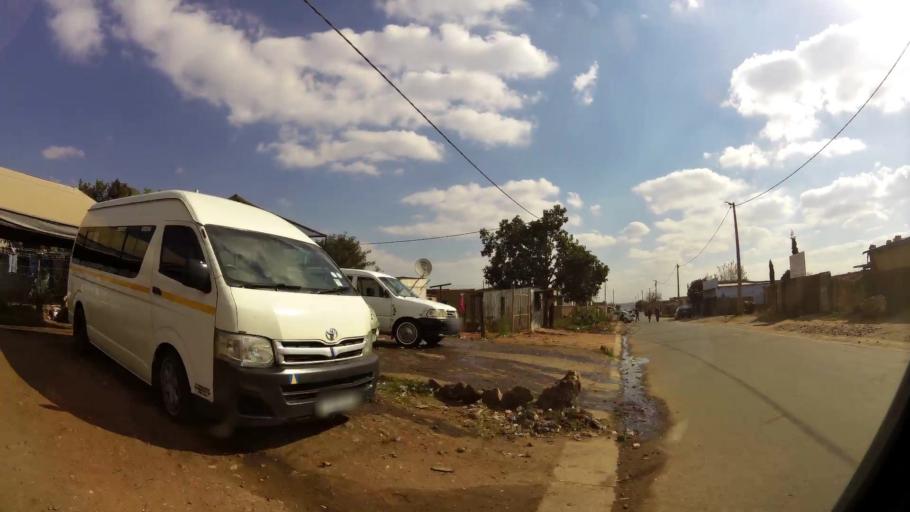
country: ZA
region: Gauteng
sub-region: Ekurhuleni Metropolitan Municipality
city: Tembisa
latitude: -25.9891
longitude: 28.2266
